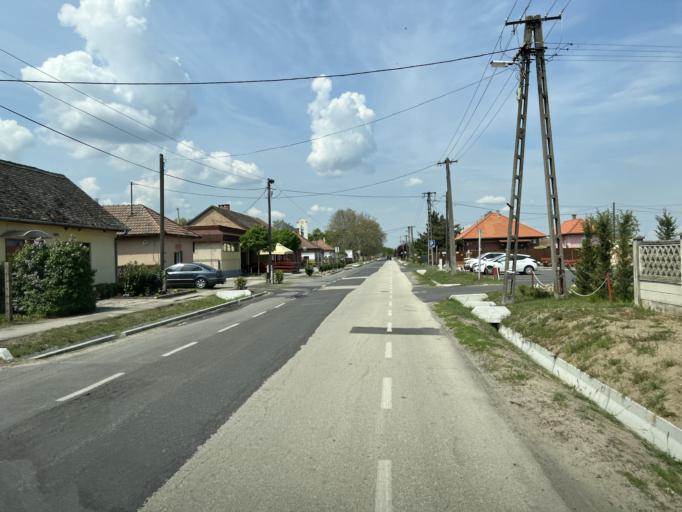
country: HU
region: Pest
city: Cegled
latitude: 47.1021
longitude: 19.7990
